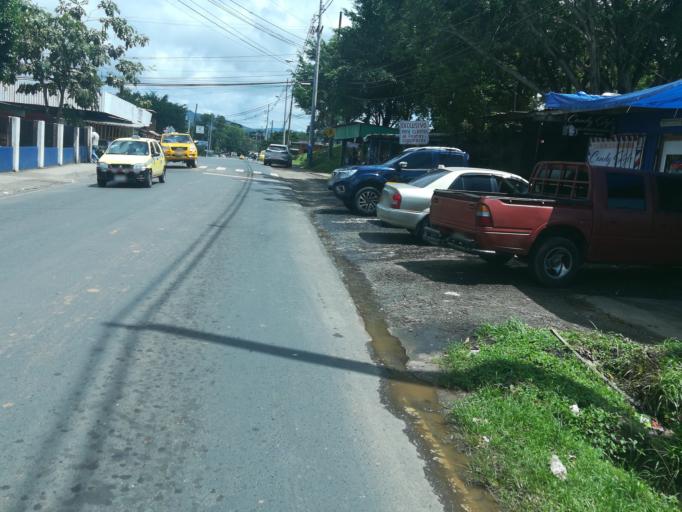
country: PA
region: Panama
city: Tocumen
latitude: 9.0938
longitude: -79.4069
